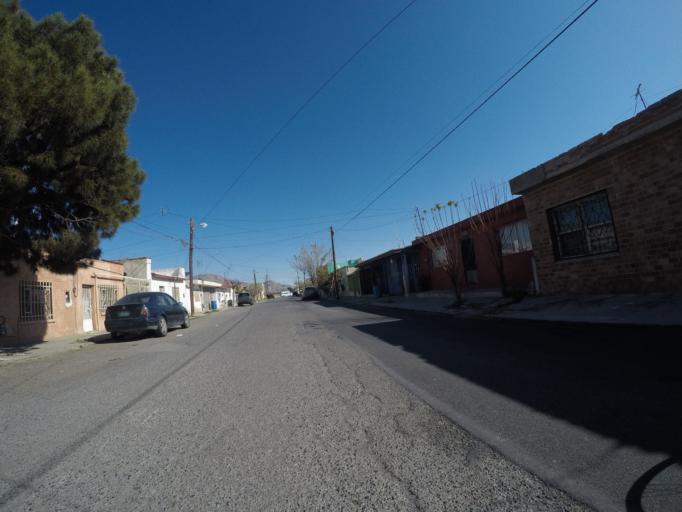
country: MX
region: Chihuahua
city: Ciudad Juarez
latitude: 31.7462
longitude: -106.4715
